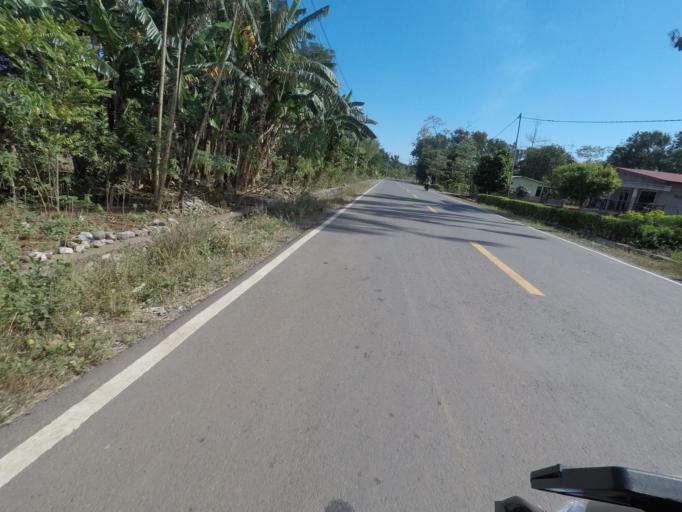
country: TL
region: Bobonaro
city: Maliana
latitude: -8.9609
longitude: 125.2151
